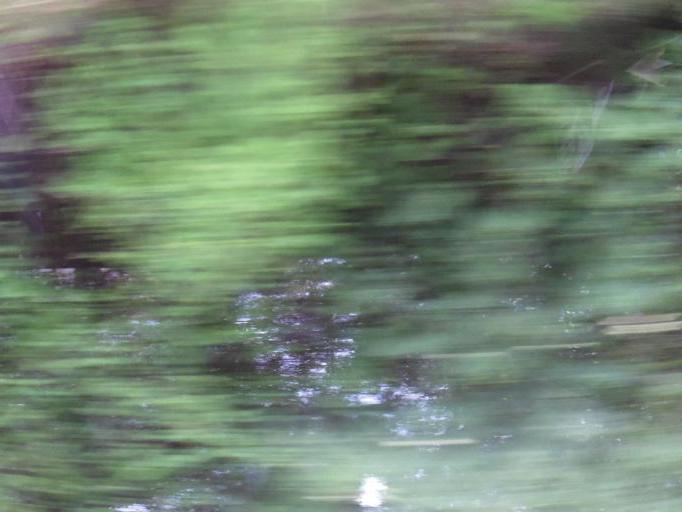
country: US
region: Florida
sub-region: Clay County
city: Bellair-Meadowbrook Terrace
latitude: 30.1962
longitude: -81.7184
